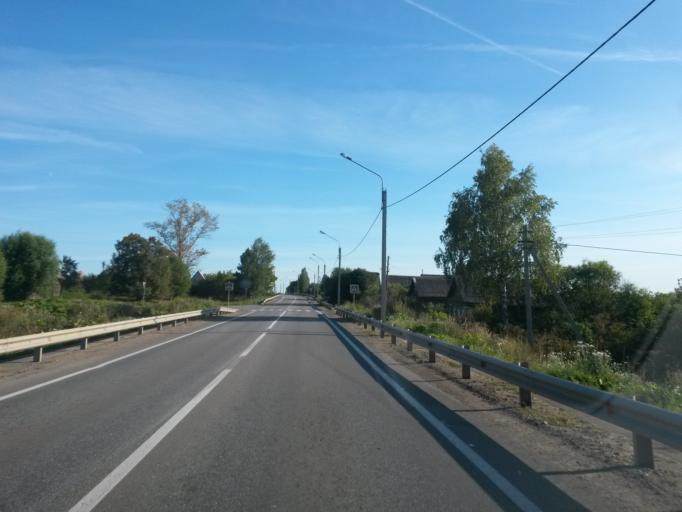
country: RU
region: Jaroslavl
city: Gavrilov-Yam
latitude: 57.3507
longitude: 39.9087
